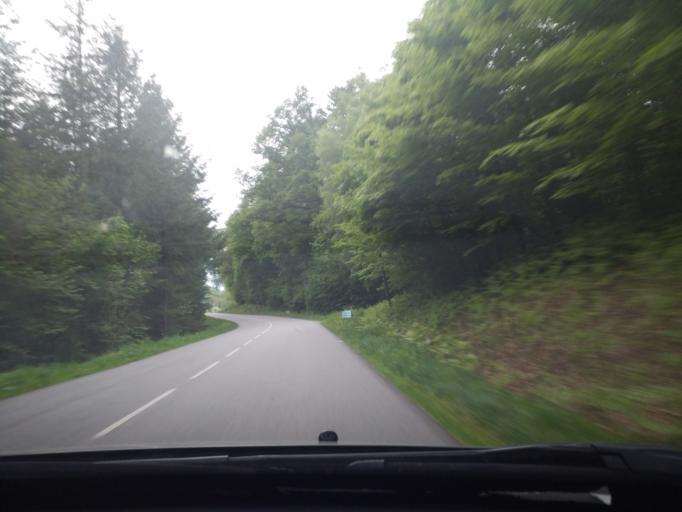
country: FR
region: Lorraine
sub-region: Departement des Vosges
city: Bains-les-Bains
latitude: 48.0314
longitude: 6.1936
